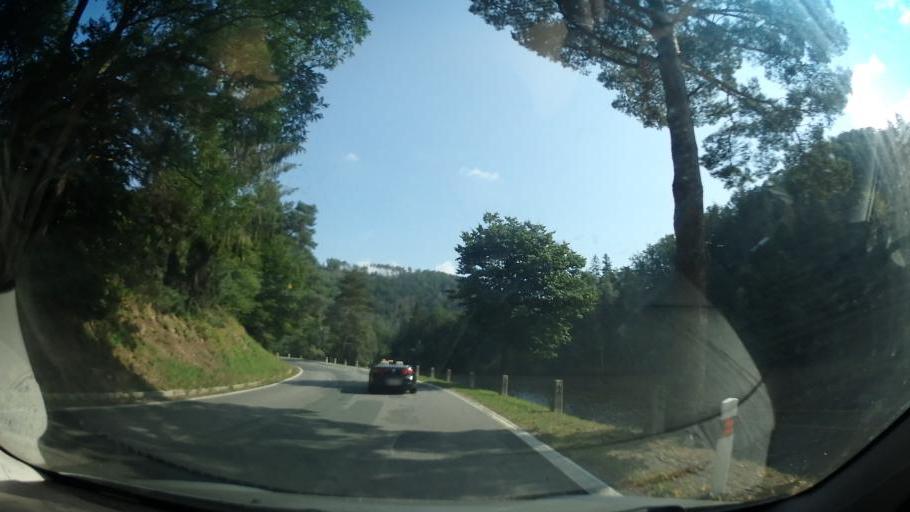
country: CZ
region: Vysocina
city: Bystrice nad Pernstejnem
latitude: 49.5471
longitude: 16.3355
